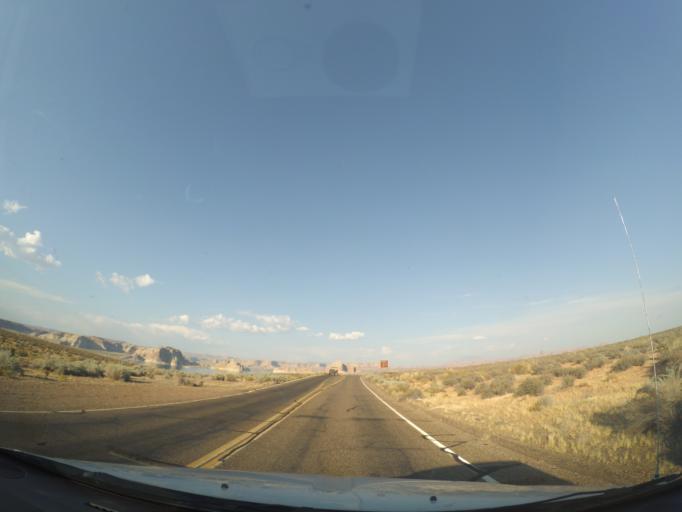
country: US
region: Arizona
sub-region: Coconino County
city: Page
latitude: 36.9934
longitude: -111.5050
